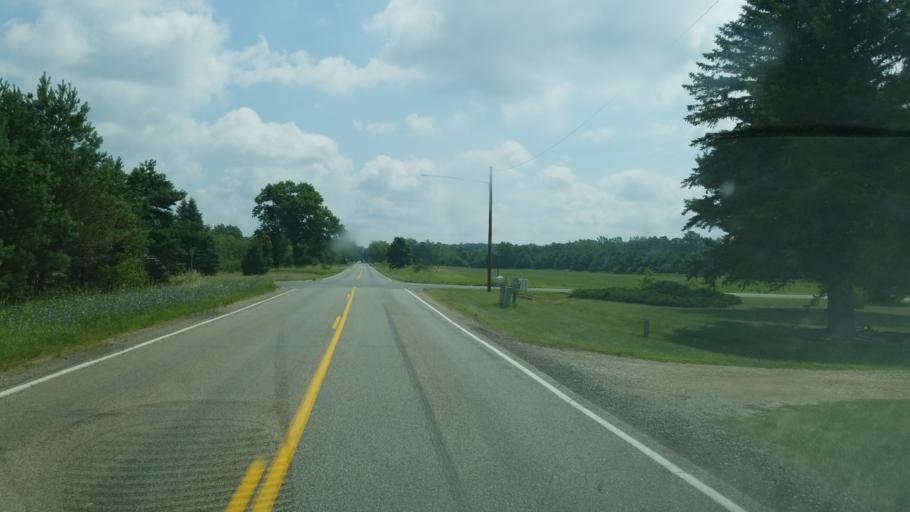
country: US
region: Michigan
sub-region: Kent County
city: Cedar Springs
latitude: 43.2203
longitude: -85.5115
